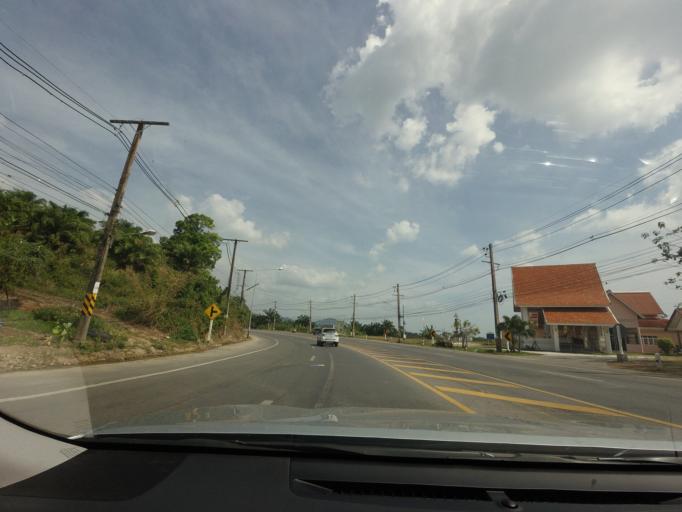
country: TH
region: Phangnga
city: Ban Ao Nang
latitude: 8.0516
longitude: 98.7722
